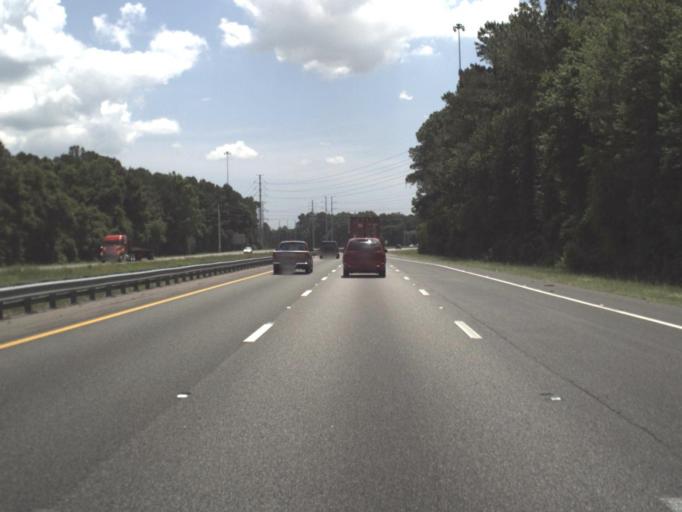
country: US
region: Florida
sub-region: Duval County
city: Jacksonville
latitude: 30.4560
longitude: -81.6286
